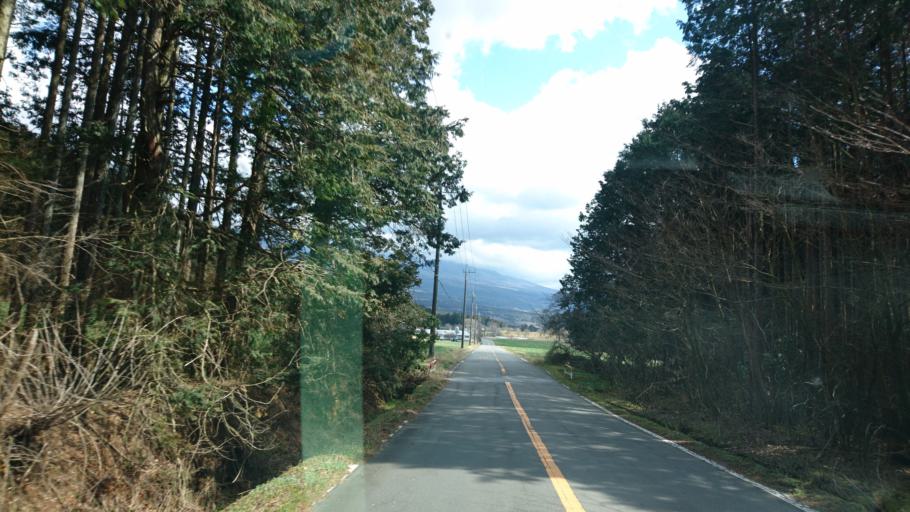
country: JP
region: Yamanashi
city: Fujikawaguchiko
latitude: 35.3810
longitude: 138.5906
